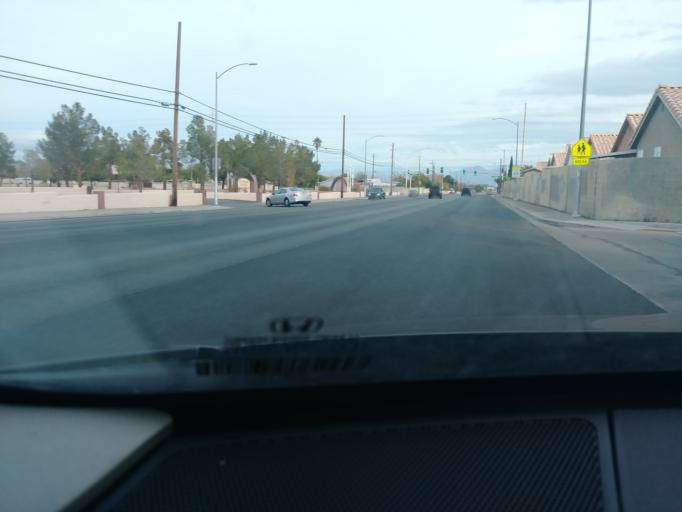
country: US
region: Nevada
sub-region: Clark County
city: Spring Valley
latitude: 36.1809
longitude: -115.2168
